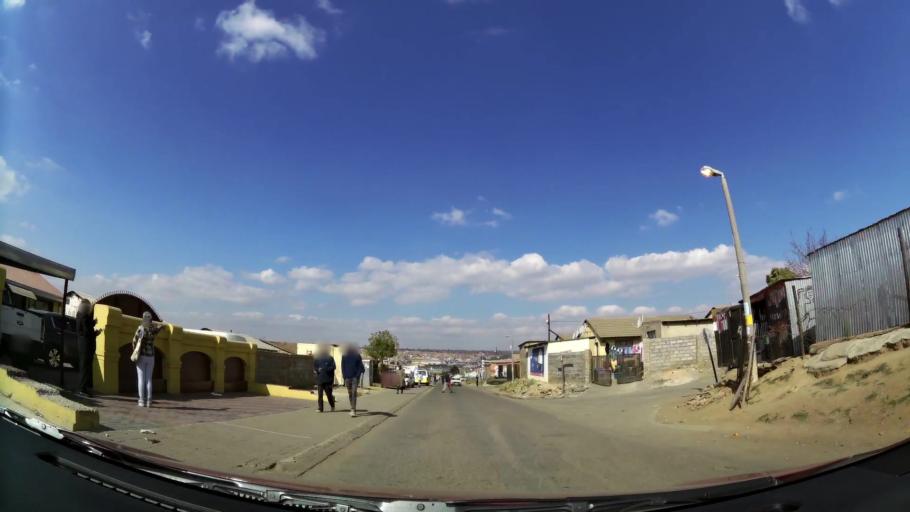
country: ZA
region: Gauteng
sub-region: Ekurhuleni Metropolitan Municipality
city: Tembisa
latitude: -26.0283
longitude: 28.1869
